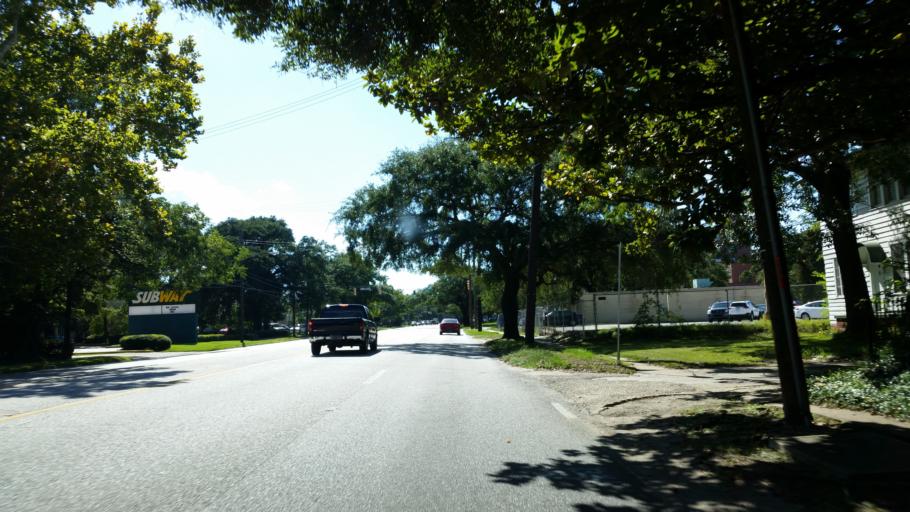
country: US
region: Alabama
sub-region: Mobile County
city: Mobile
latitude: 30.6926
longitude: -88.0695
